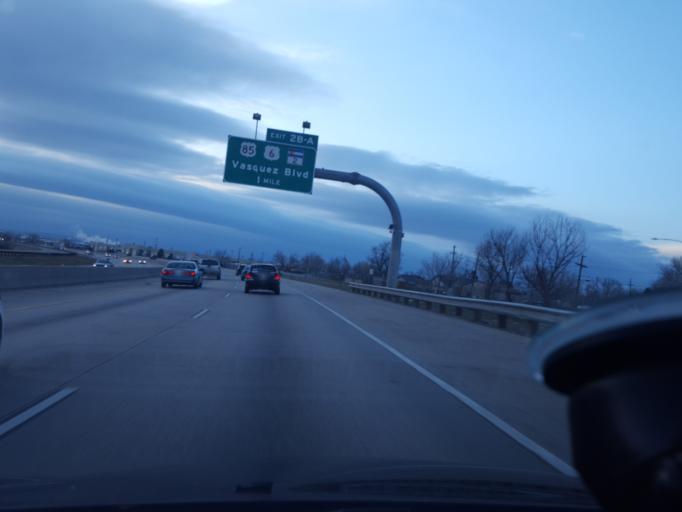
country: US
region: Colorado
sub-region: Adams County
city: Commerce City
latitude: 39.7936
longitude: -104.9139
